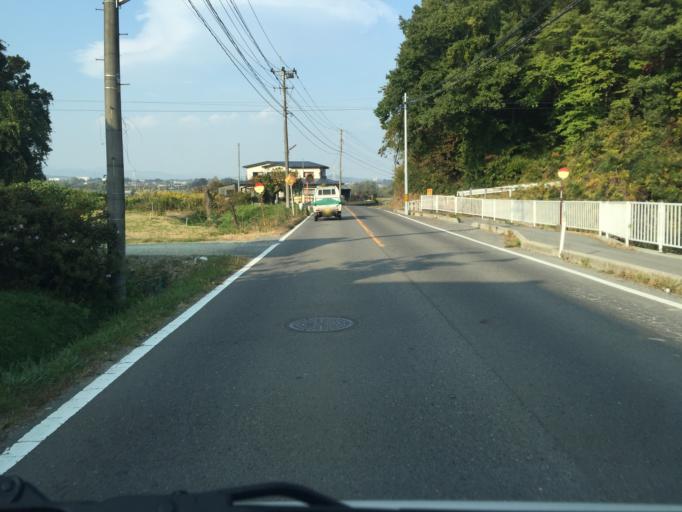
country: JP
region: Fukushima
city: Motomiya
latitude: 37.4717
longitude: 140.3894
